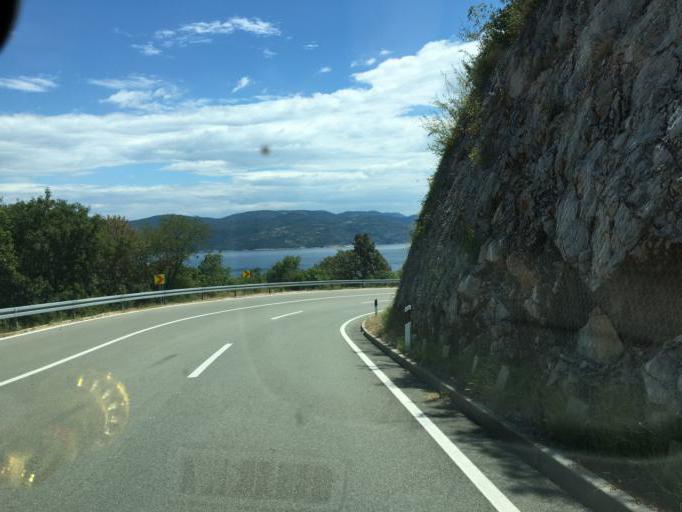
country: HR
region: Istarska
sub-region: Grad Labin
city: Rabac
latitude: 45.1451
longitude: 14.2200
